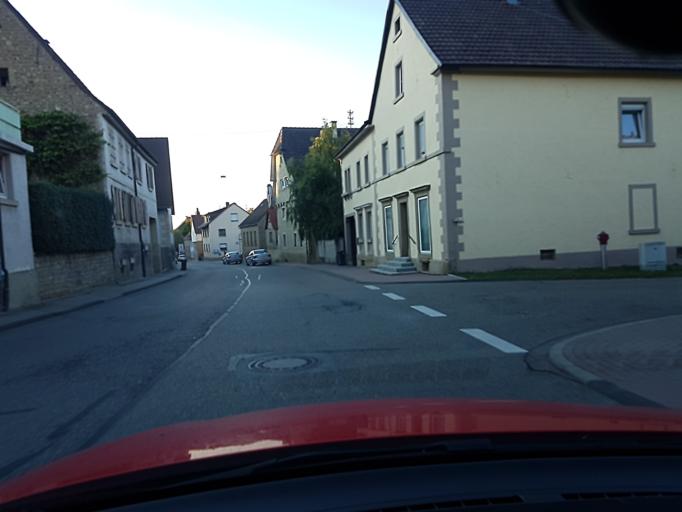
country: DE
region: Baden-Wuerttemberg
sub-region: Regierungsbezirk Stuttgart
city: Eppingen
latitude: 49.0985
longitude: 8.9018
